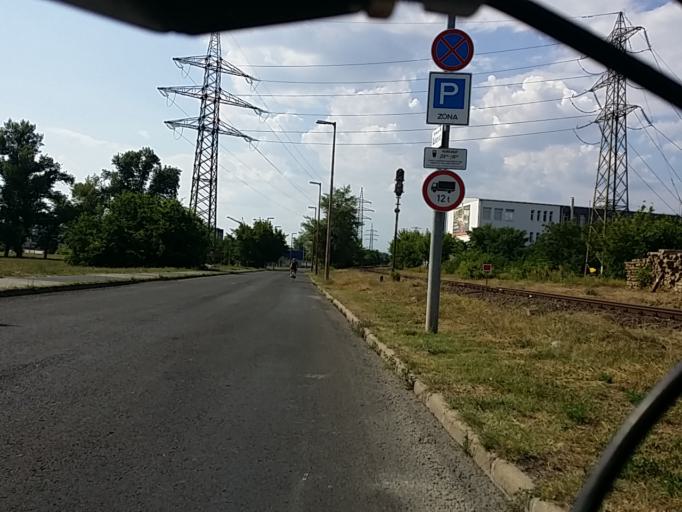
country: HU
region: Budapest
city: Budapest IV. keruelet
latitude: 47.5542
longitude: 19.0837
